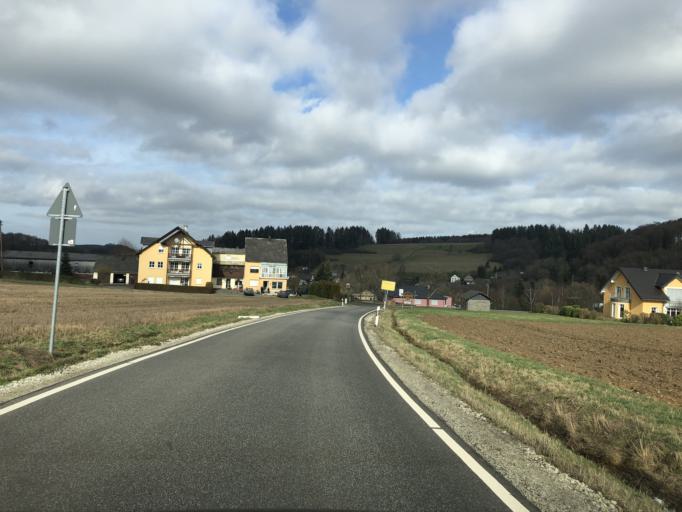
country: DE
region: Rheinland-Pfalz
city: Kommen
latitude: 49.8612
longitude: 7.1622
